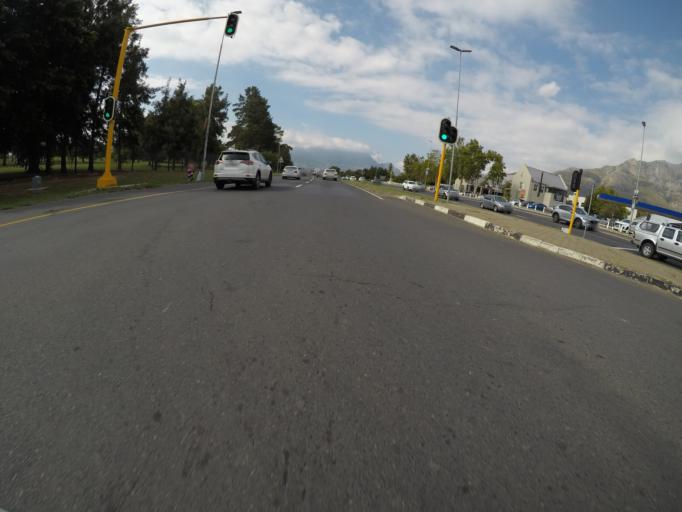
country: ZA
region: Western Cape
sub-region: Cape Winelands District Municipality
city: Stellenbosch
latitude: -33.9630
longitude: 18.8505
